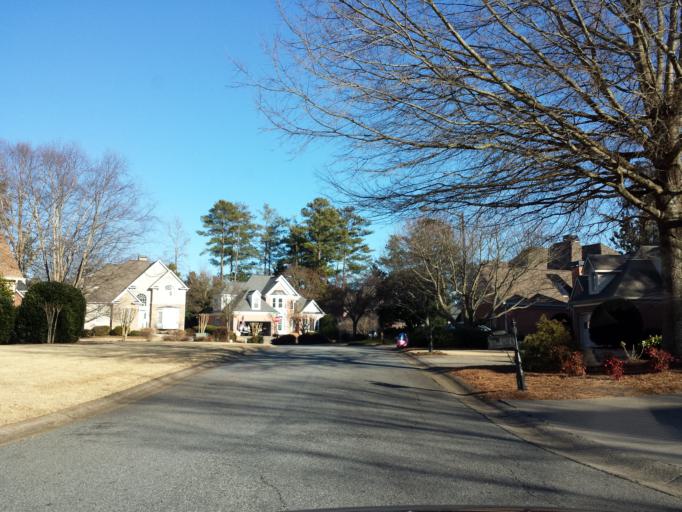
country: US
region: Georgia
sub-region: Cobb County
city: Smyrna
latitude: 33.9417
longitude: -84.4667
